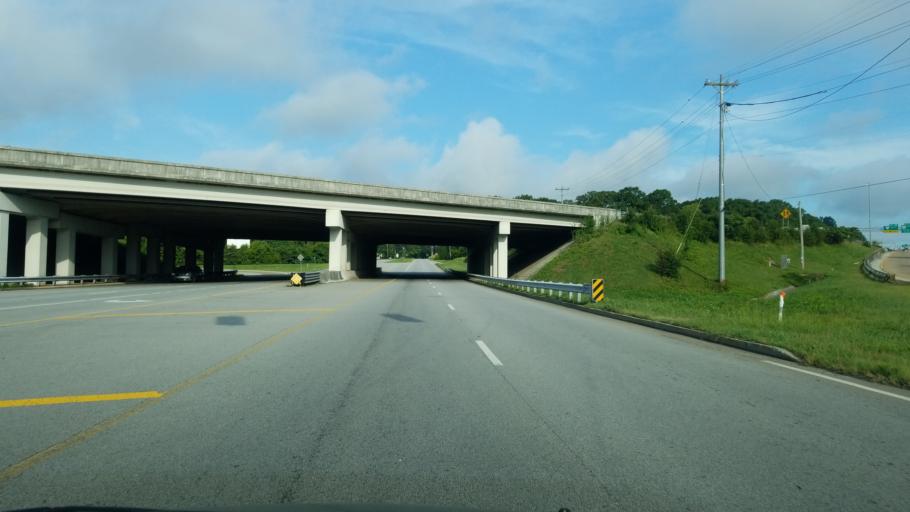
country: US
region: Tennessee
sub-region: Hamilton County
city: East Chattanooga
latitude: 35.0751
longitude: -85.1982
